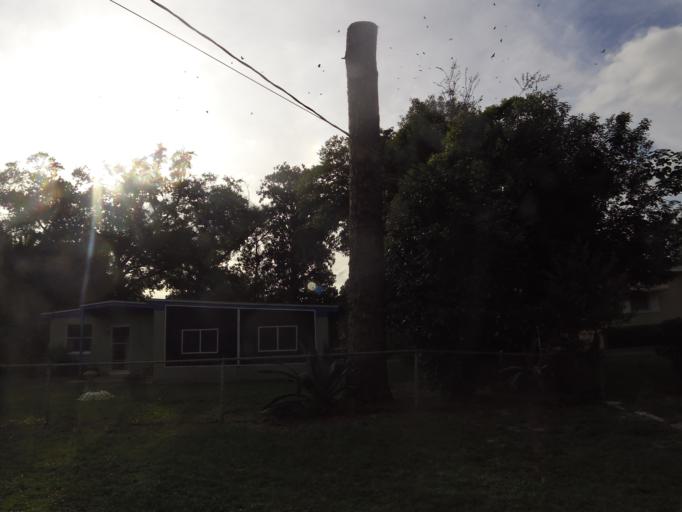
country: US
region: Florida
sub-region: Duval County
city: Jacksonville
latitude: 30.4274
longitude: -81.6751
